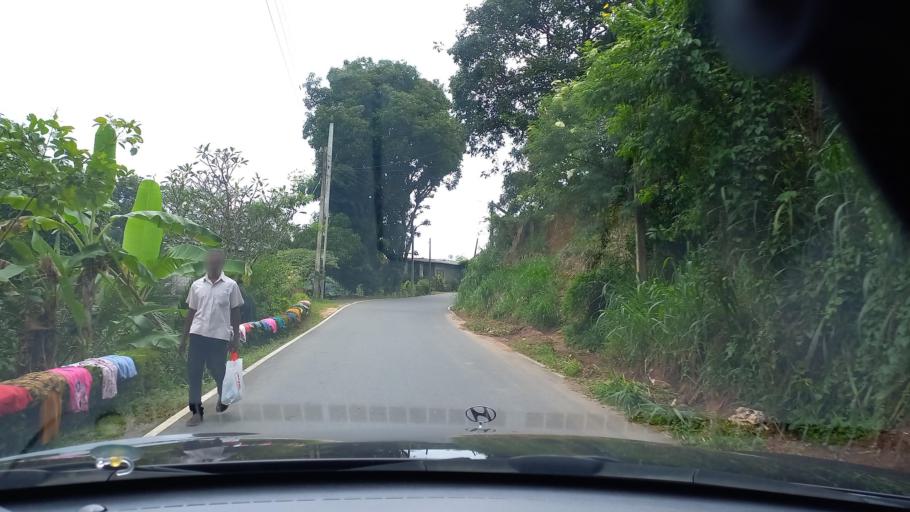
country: LK
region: Central
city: Gampola
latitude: 7.2261
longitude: 80.6059
